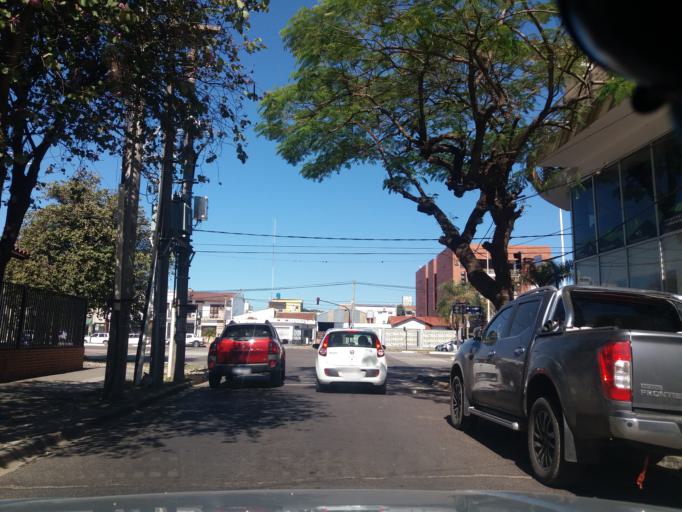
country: AR
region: Corrientes
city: Corrientes
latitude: -27.4743
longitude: -58.8448
